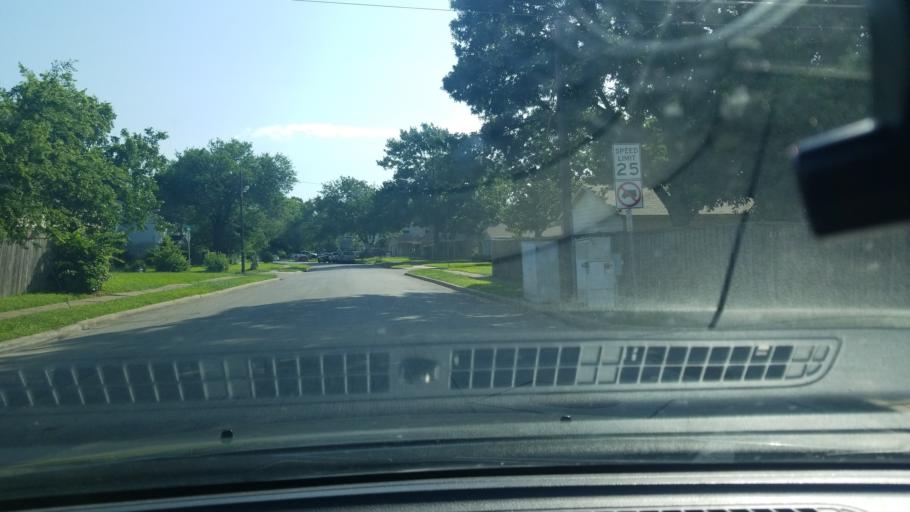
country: US
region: Texas
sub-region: Dallas County
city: Mesquite
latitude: 32.8206
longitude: -96.6404
